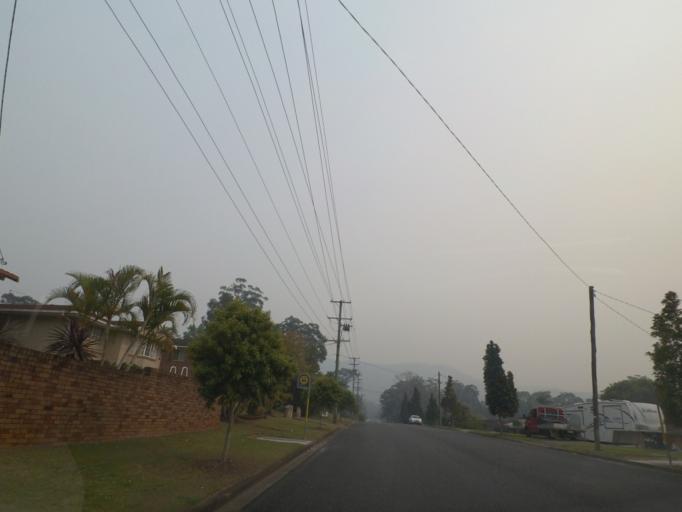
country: AU
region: New South Wales
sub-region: Coffs Harbour
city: Coffs Harbour
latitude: -30.2820
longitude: 153.1033
